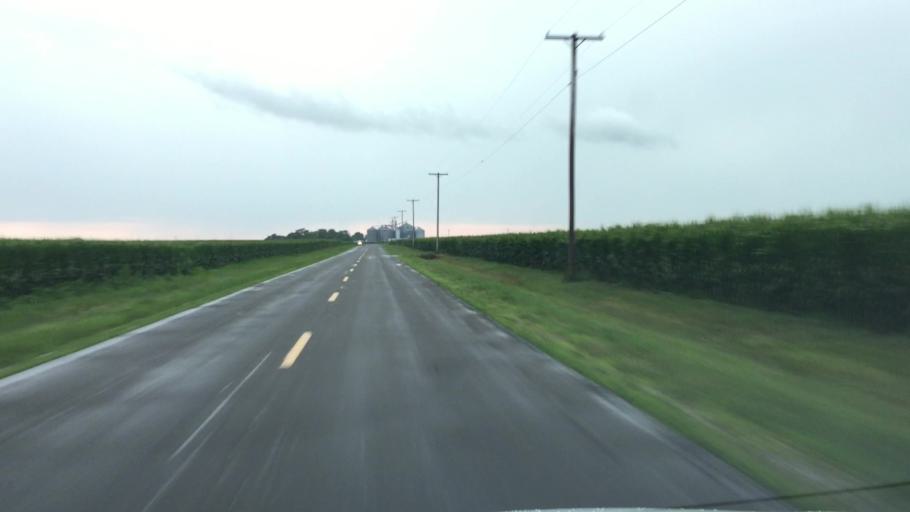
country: US
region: Illinois
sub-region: Hancock County
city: Carthage
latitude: 40.5203
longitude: -91.1493
